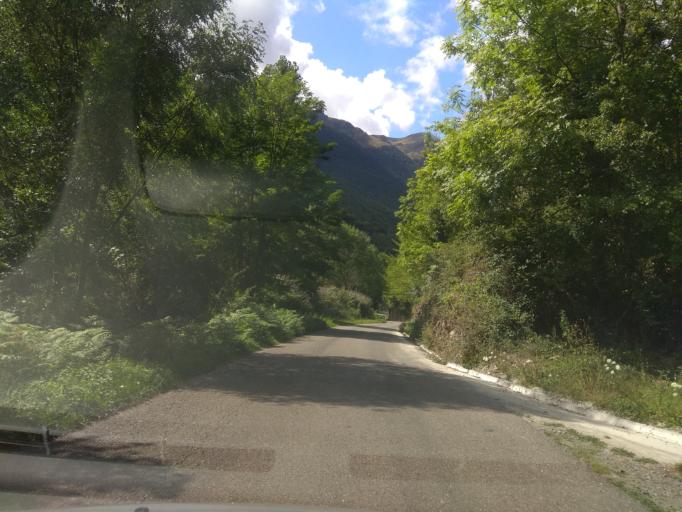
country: ES
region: Catalonia
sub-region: Provincia de Lleida
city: Vielha
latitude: 42.7318
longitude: 0.7250
